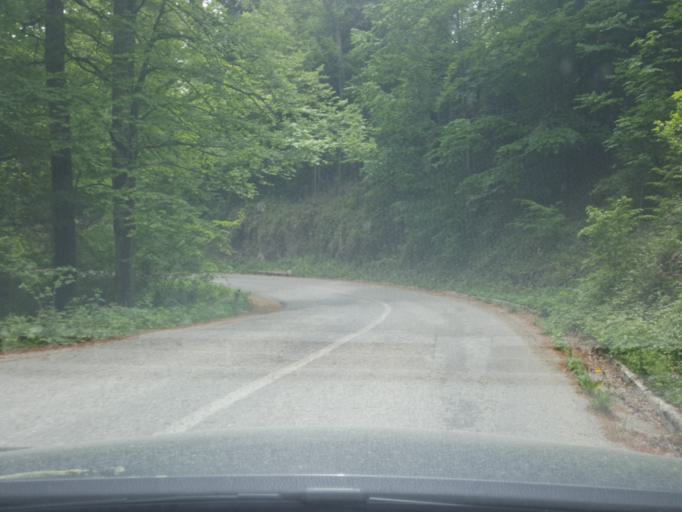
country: RS
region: Central Serbia
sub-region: Zlatiborski Okrug
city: Bajina Basta
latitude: 43.9160
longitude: 19.4939
